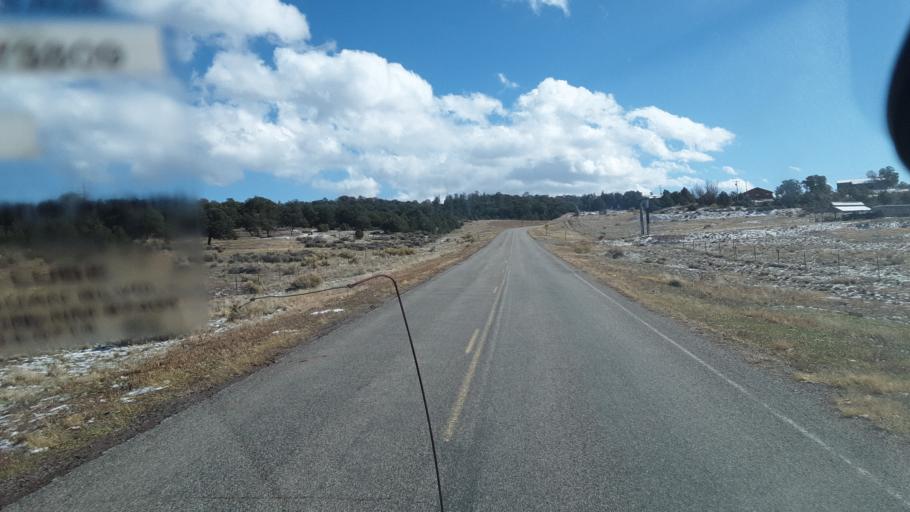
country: US
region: New Mexico
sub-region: Rio Arriba County
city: Santa Teresa
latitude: 36.2324
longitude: -106.8351
